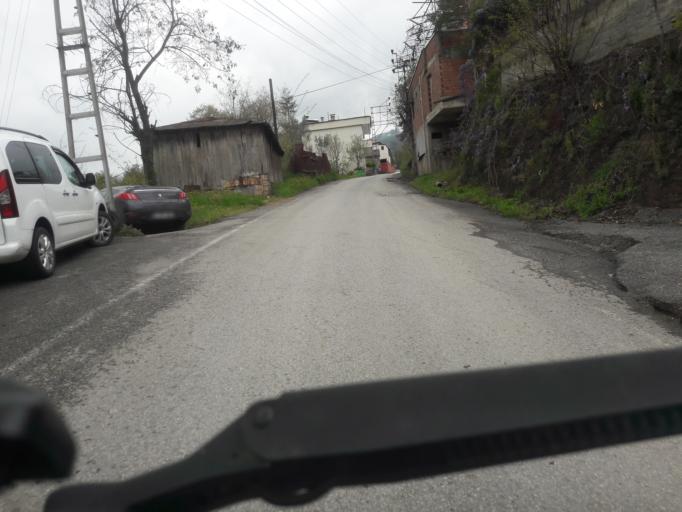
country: TR
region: Trabzon
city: Derecik
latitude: 40.9440
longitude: 39.4958
